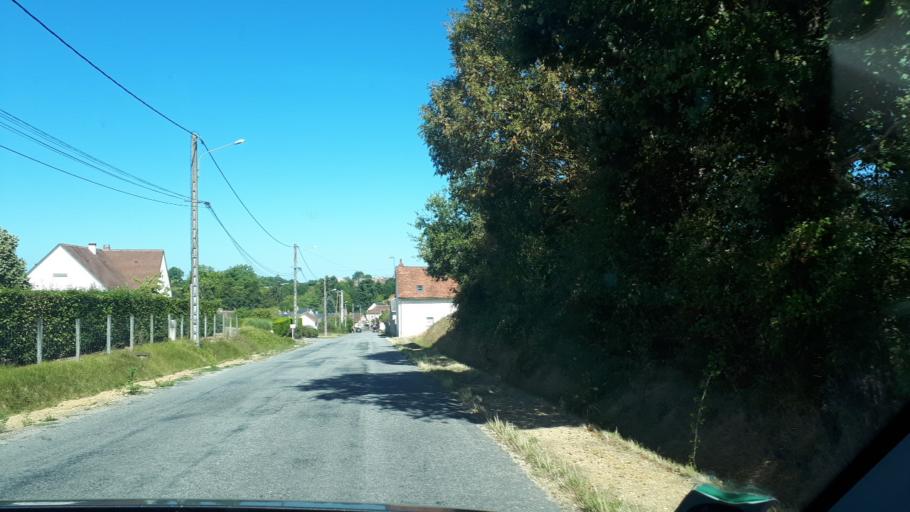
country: FR
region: Centre
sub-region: Departement du Loiret
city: Autry-le-Chatel
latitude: 47.5938
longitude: 2.6059
